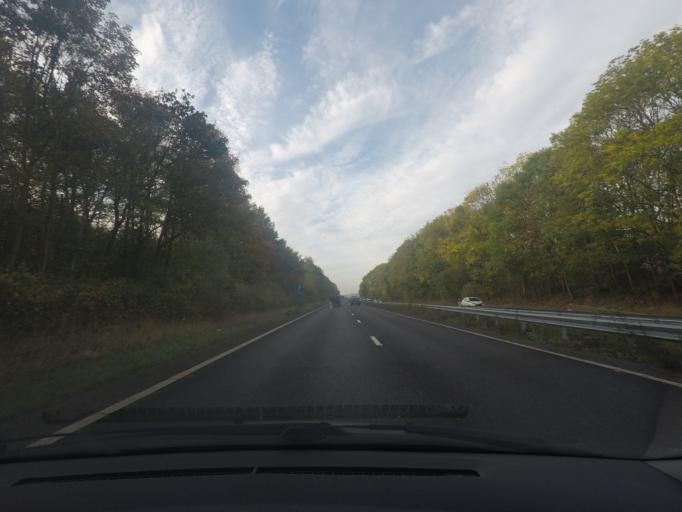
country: GB
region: England
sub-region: North Yorkshire
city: Tadcaster
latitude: 53.8849
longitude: -1.2501
